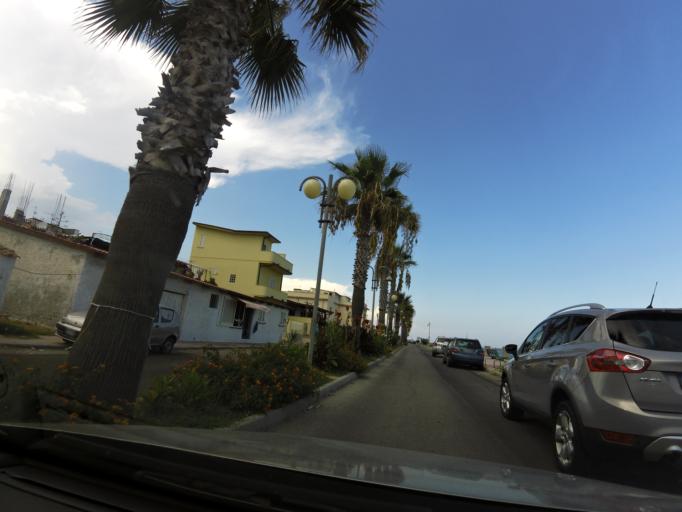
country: IT
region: Calabria
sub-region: Provincia di Reggio Calabria
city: Monasterace Marina
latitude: 38.4343
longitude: 16.5746
